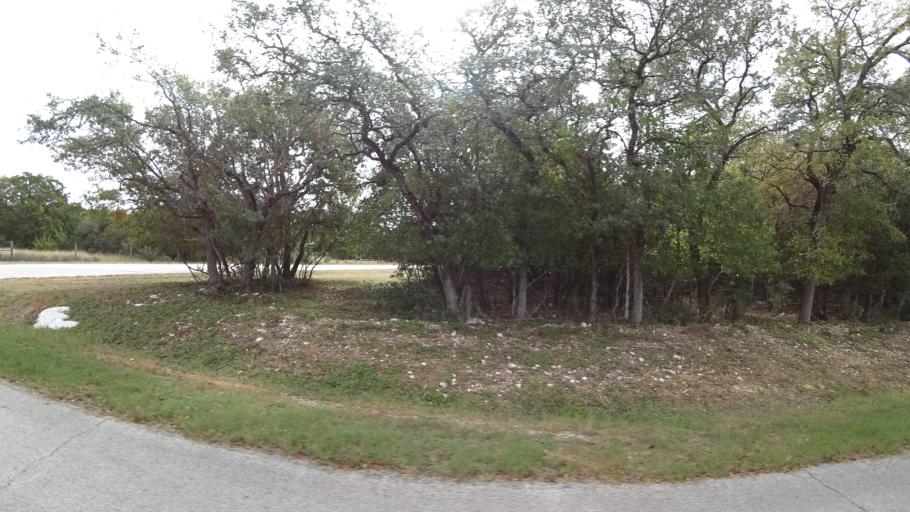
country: US
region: Texas
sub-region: Travis County
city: Shady Hollow
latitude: 30.1377
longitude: -97.8835
